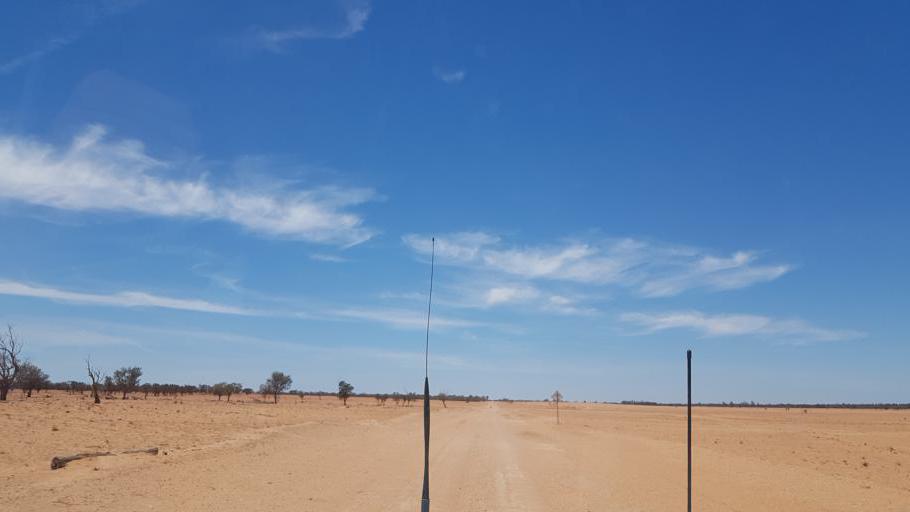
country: AU
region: New South Wales
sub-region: Wentworth
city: Dareton
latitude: -33.3493
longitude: 141.4639
